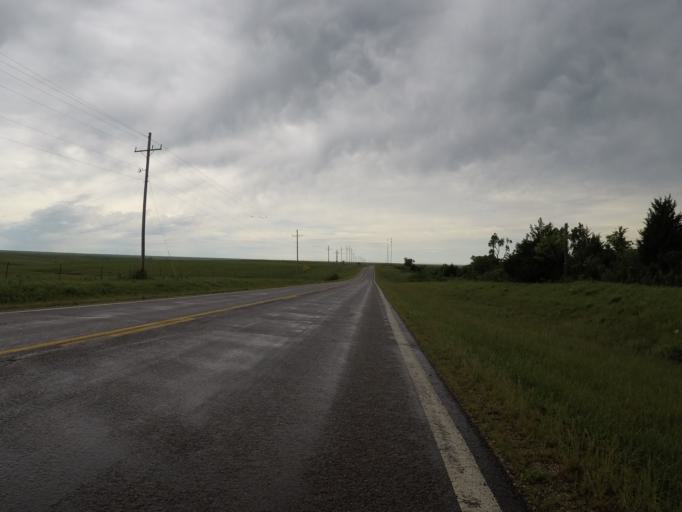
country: US
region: Kansas
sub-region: Wabaunsee County
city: Alma
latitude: 38.8652
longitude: -96.1229
